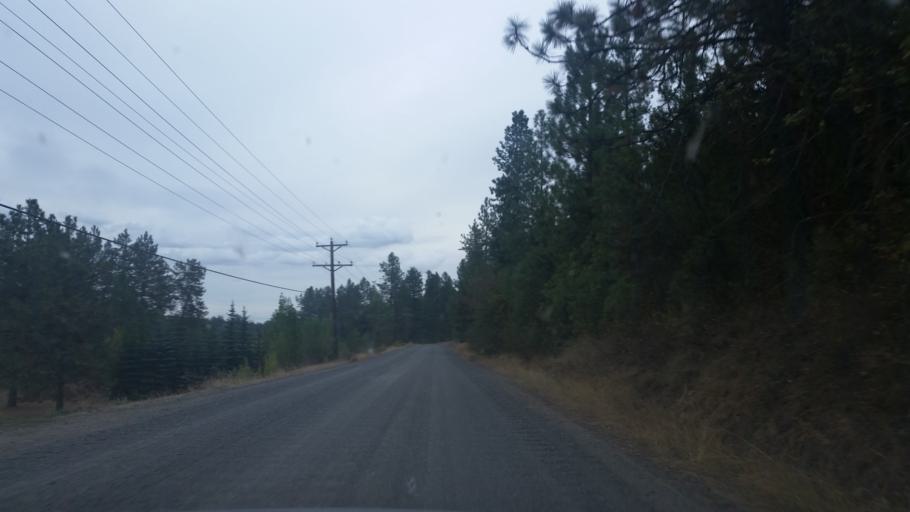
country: US
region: Washington
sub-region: Spokane County
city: Cheney
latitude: 47.5385
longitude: -117.5888
